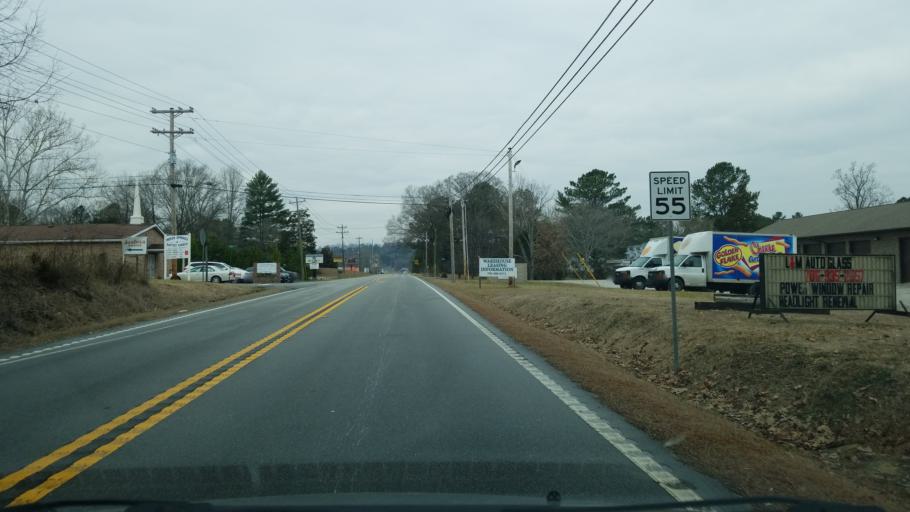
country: US
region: Georgia
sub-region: Catoosa County
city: Indian Springs
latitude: 34.9619
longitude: -85.1700
